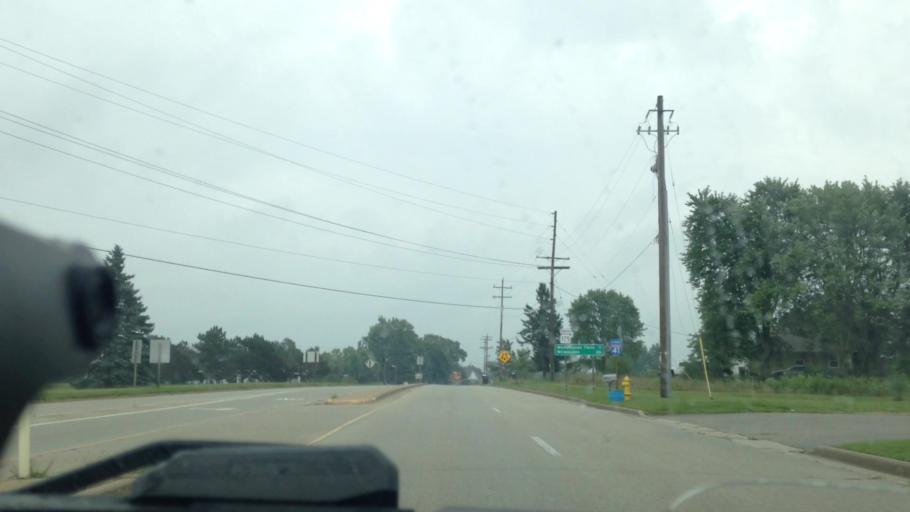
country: US
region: Wisconsin
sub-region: Washington County
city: Slinger
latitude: 43.3243
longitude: -88.2719
